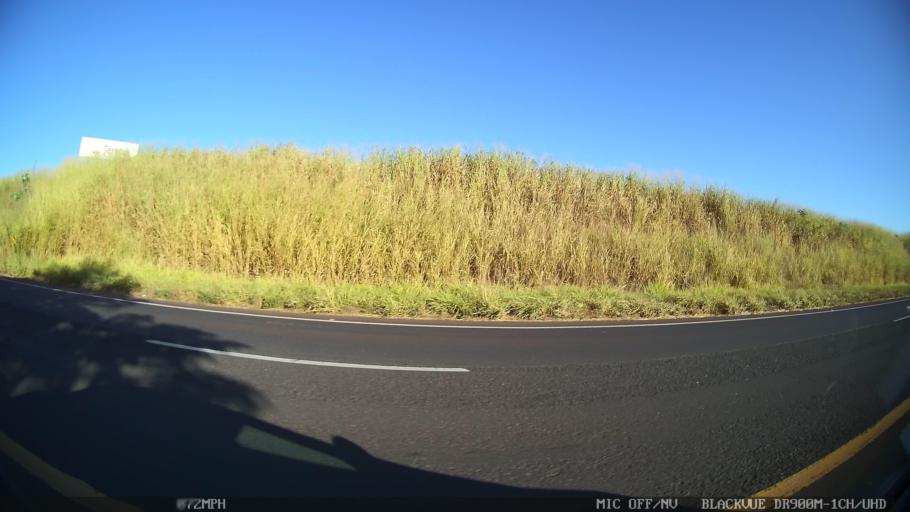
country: BR
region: Sao Paulo
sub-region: Guapiacu
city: Guapiacu
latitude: -20.7405
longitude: -49.0951
